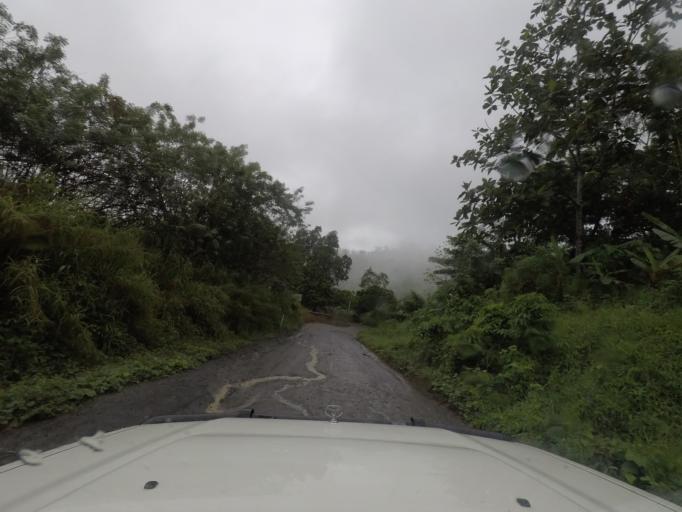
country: PG
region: Madang
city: Madang
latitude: -5.4568
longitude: 145.5003
